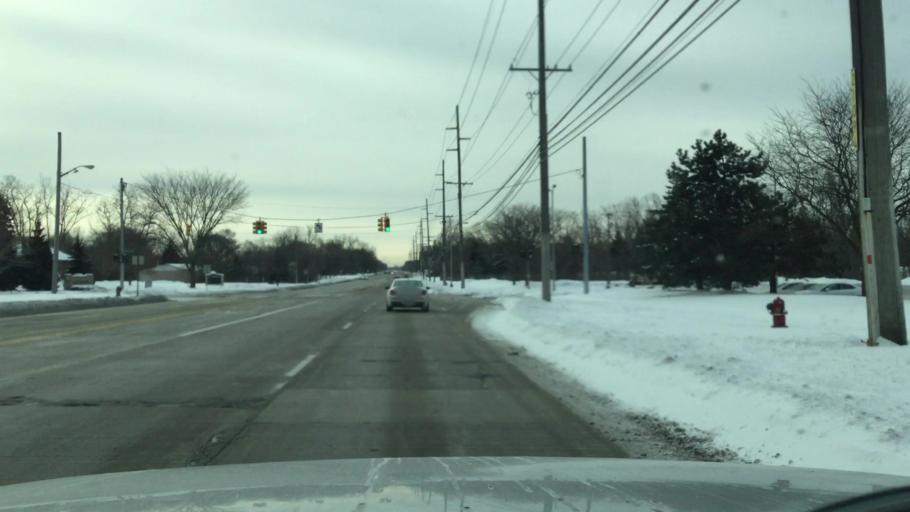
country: US
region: Michigan
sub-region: Oakland County
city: Troy
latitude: 42.6024
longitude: -83.1296
